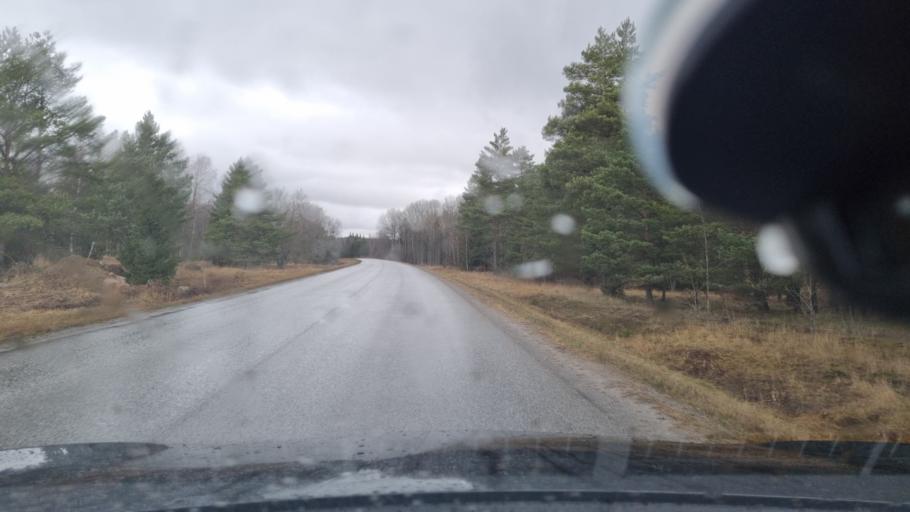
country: SE
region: Stockholm
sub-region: Upplands-Bro Kommun
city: Kungsaengen
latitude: 59.5302
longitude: 17.7499
